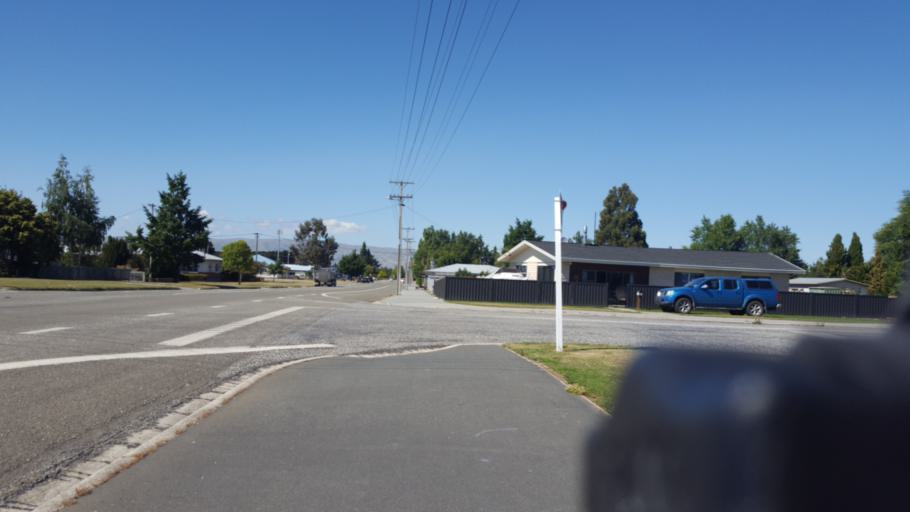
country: NZ
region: Otago
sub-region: Dunedin City
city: Dunedin
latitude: -45.1266
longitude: 170.1004
